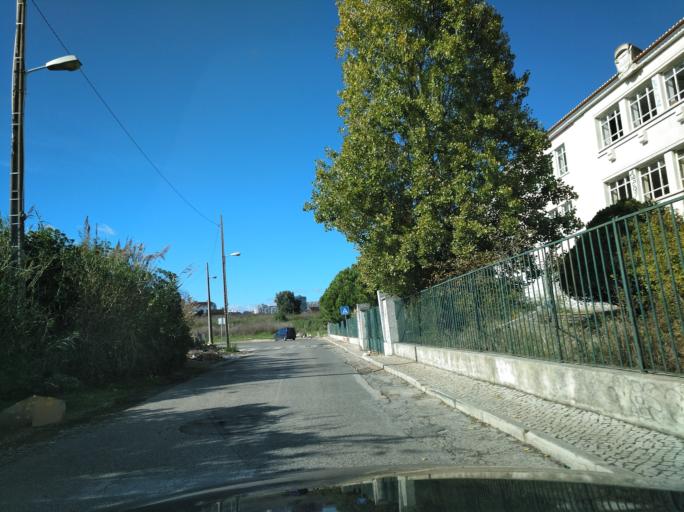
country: PT
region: Lisbon
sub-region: Lisbon
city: Lisbon
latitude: 38.7355
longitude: -9.1095
